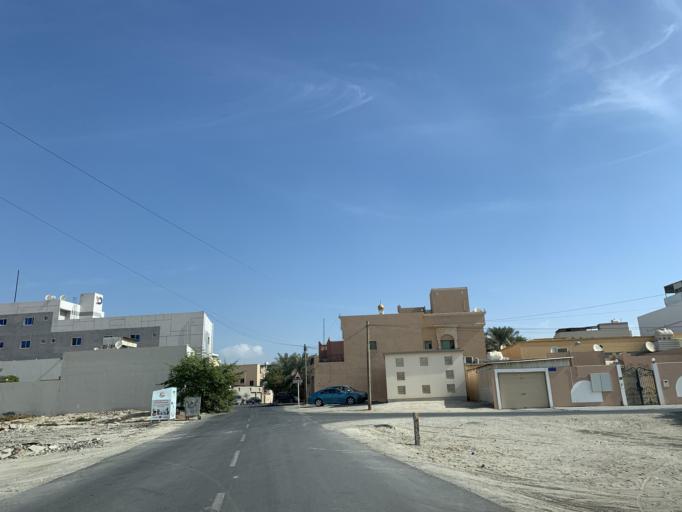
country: BH
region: Central Governorate
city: Madinat Hamad
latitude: 26.1277
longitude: 50.4741
